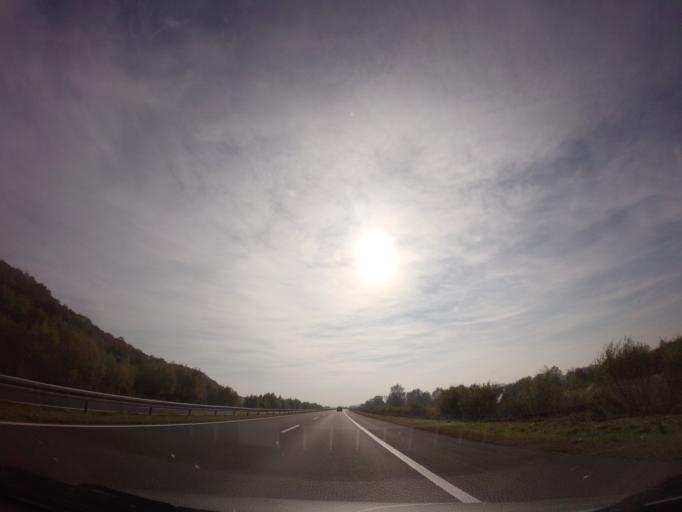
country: HR
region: Varazdinska
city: Remetinec
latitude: 46.0631
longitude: 16.2984
